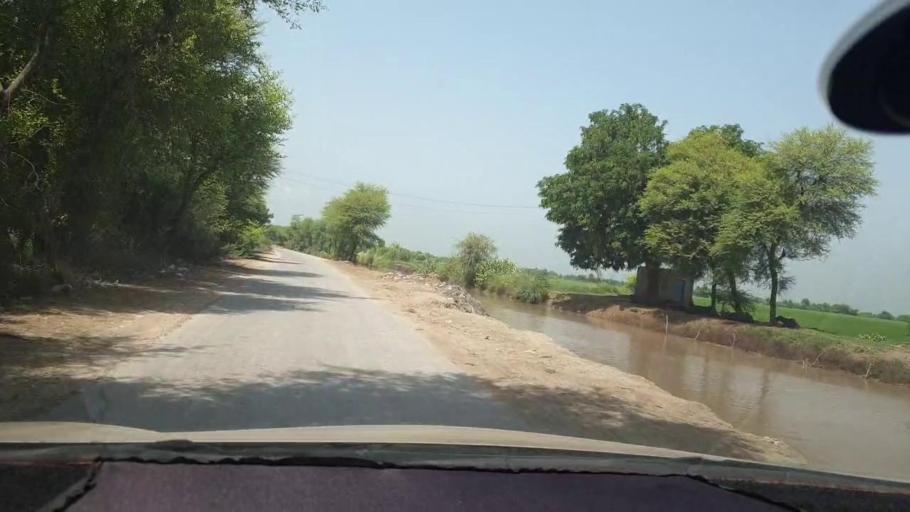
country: PK
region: Sindh
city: Kambar
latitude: 27.6353
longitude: 67.9819
